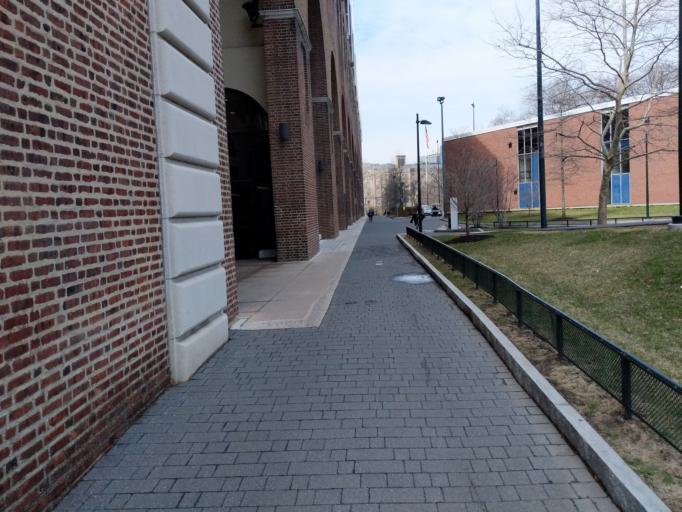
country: US
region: Pennsylvania
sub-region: Philadelphia County
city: Philadelphia
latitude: 39.9501
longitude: -75.1889
